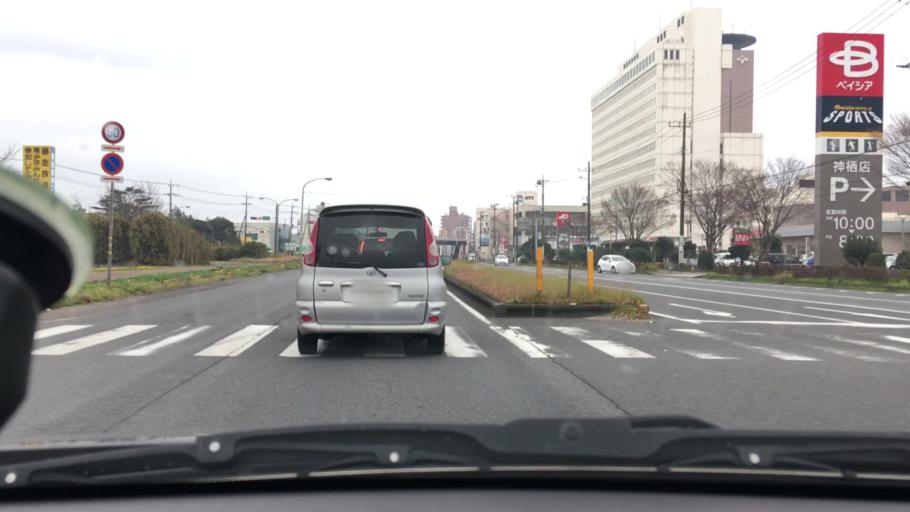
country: JP
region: Chiba
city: Omigawa
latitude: 35.9011
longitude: 140.6361
